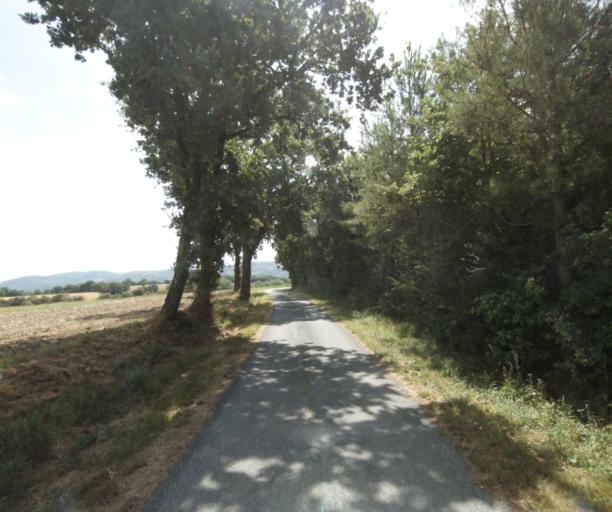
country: FR
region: Midi-Pyrenees
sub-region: Departement du Tarn
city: Dourgne
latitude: 43.4902
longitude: 2.0977
